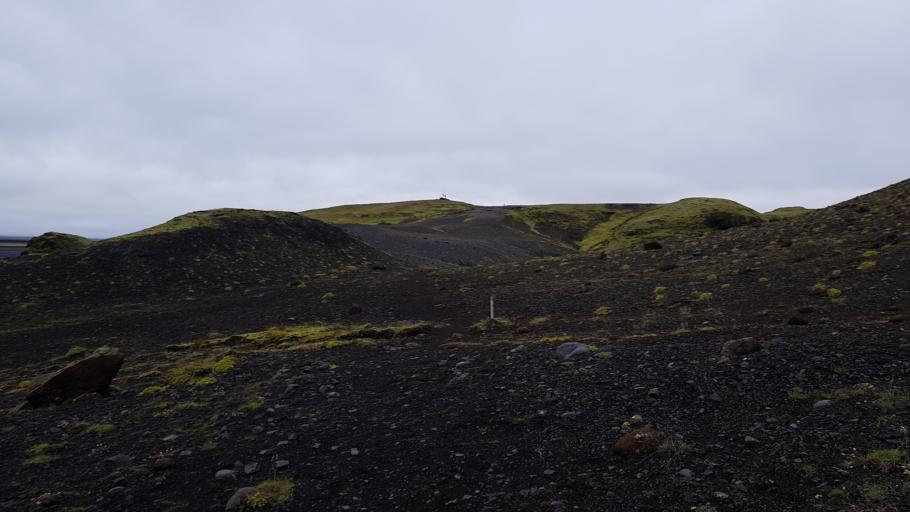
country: IS
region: South
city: Vestmannaeyjar
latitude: 63.5291
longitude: -18.8482
